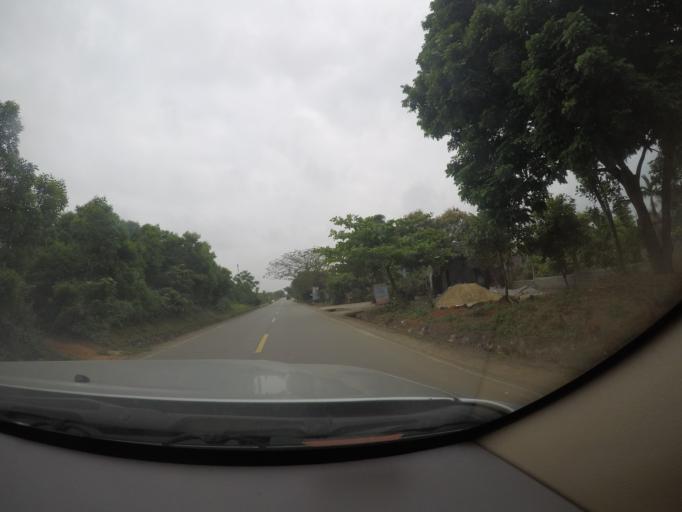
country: VN
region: Quang Binh
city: Hoan Lao
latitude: 17.5282
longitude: 106.4785
